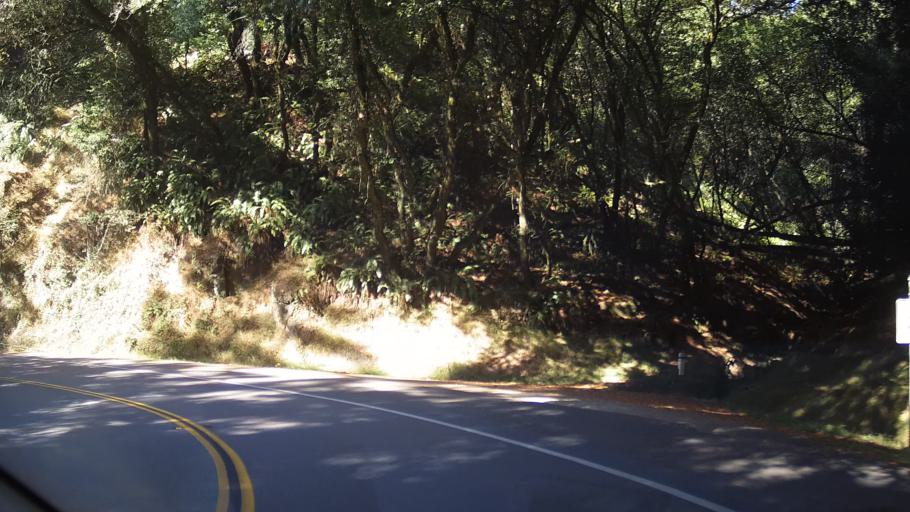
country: US
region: California
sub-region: Marin County
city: Mill Valley
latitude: 37.8990
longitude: -122.6126
